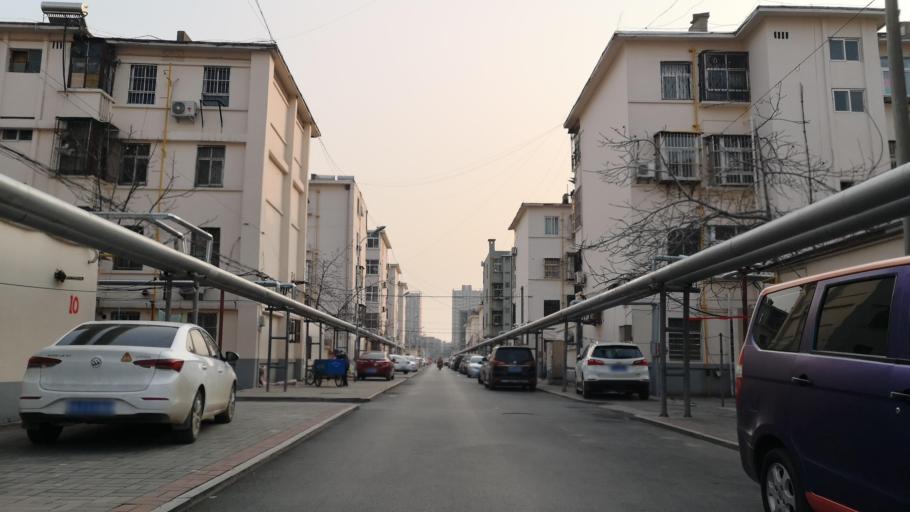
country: CN
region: Henan Sheng
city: Zhongyuanlu
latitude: 35.7684
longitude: 115.1019
